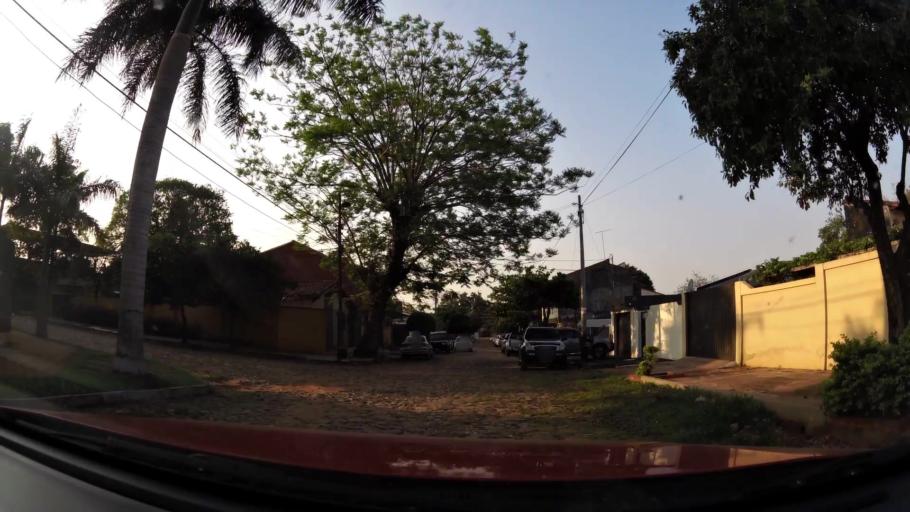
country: PY
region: Central
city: Lambare
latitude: -25.3453
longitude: -57.6063
